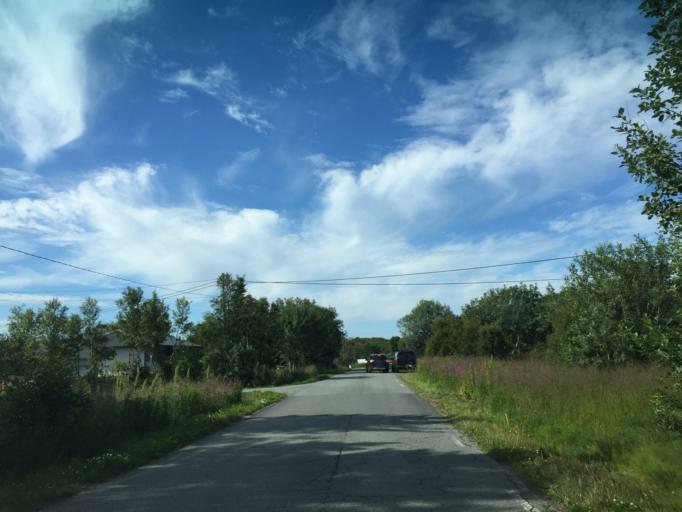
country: NO
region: Nordland
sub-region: Vagan
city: Kabelvag
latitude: 68.3917
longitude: 14.4370
